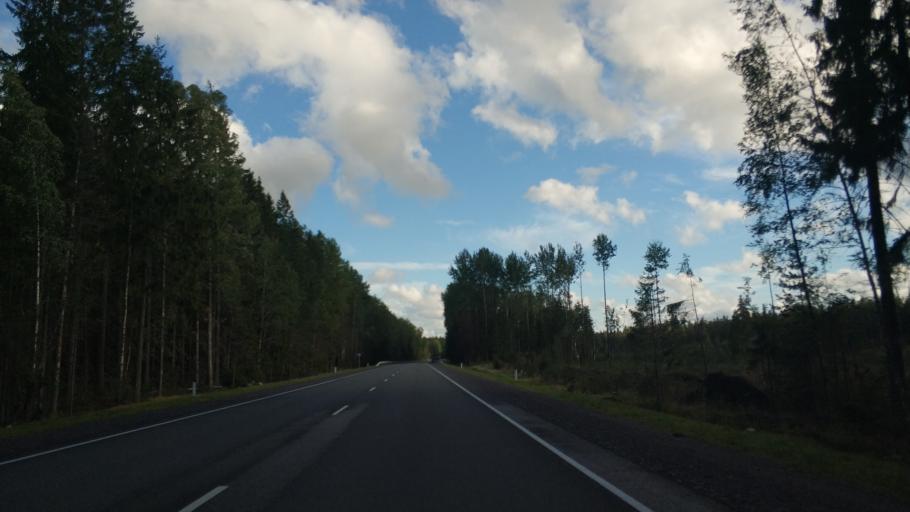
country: RU
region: Leningrad
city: Priozersk
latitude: 60.9142
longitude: 30.1567
